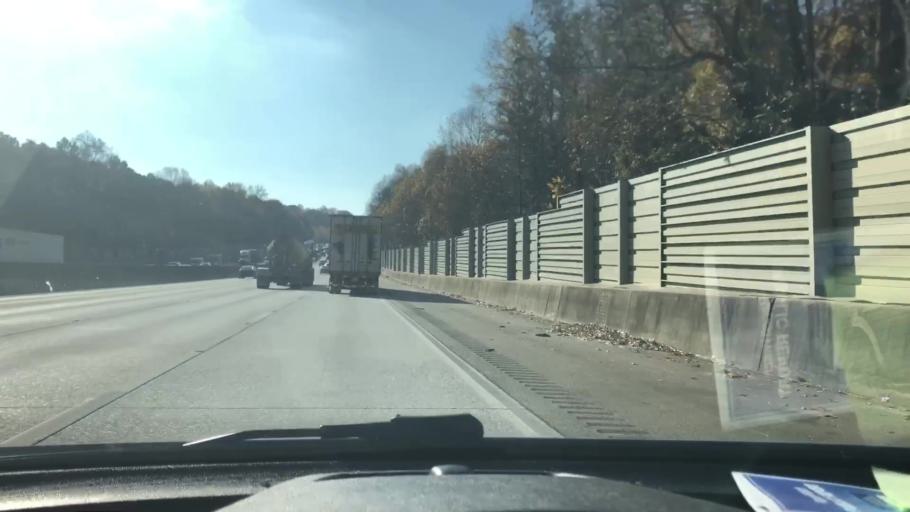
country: US
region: Georgia
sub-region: DeKalb County
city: Tucker
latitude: 33.8597
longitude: -84.2476
